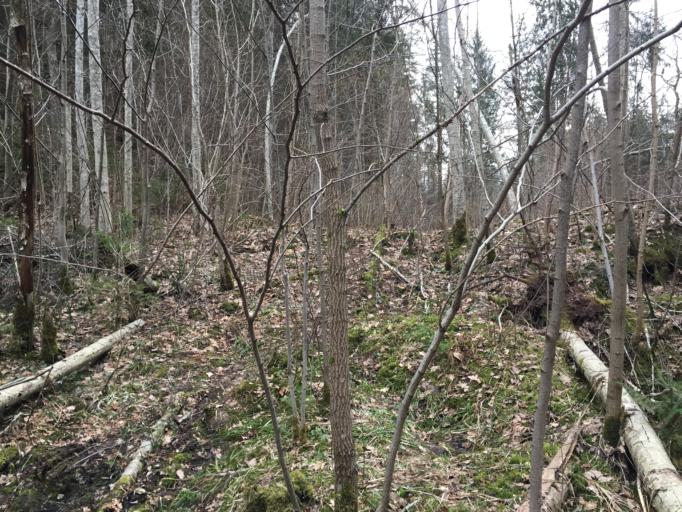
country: LV
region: Sigulda
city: Sigulda
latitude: 57.1284
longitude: 24.8126
